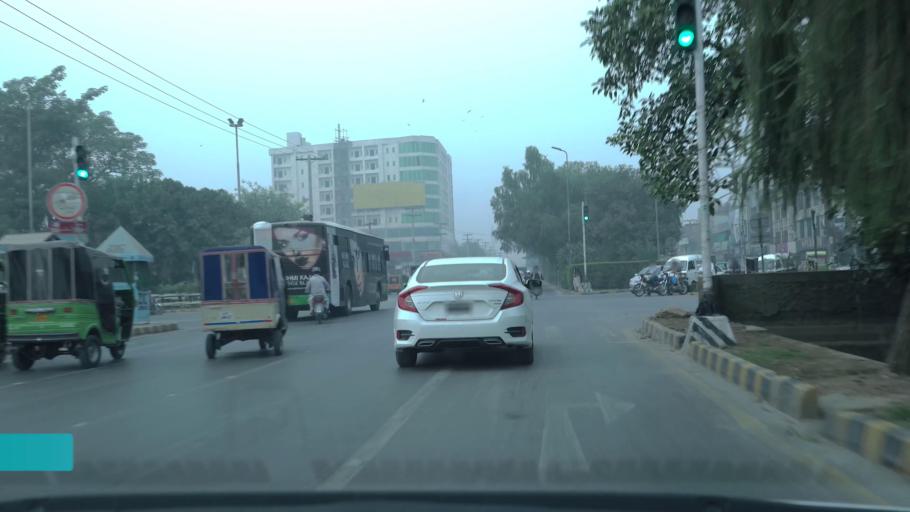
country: PK
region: Punjab
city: Lahore
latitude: 31.4724
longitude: 74.3027
